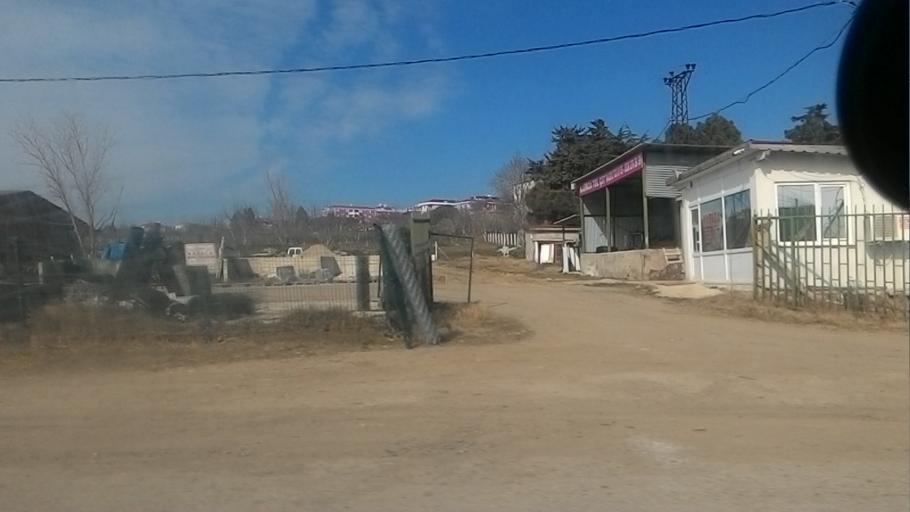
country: TR
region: Istanbul
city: Canta
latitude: 41.0770
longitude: 28.0793
